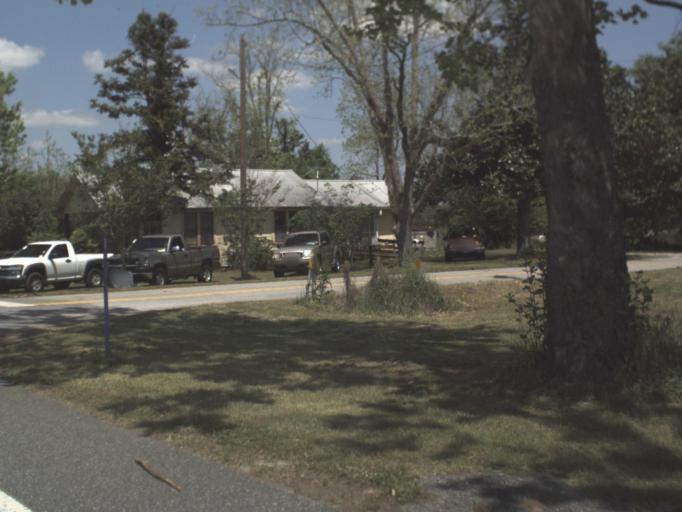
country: US
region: Florida
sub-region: Santa Rosa County
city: Point Baker
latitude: 30.8816
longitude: -87.0523
